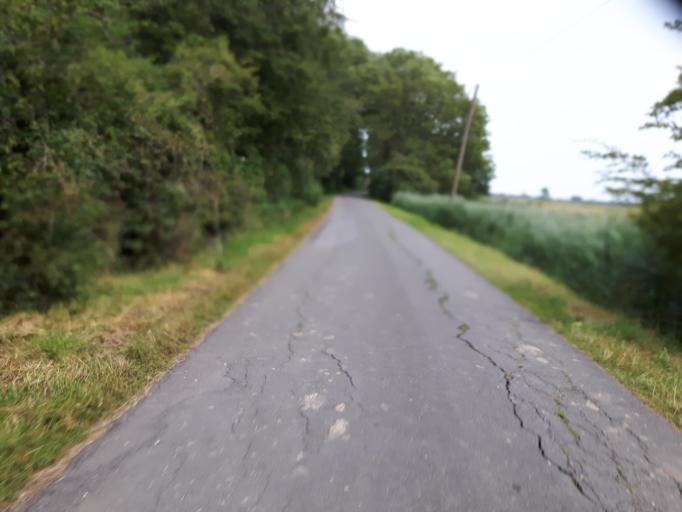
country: DE
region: Lower Saxony
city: Varel
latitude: 53.3654
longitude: 8.2068
